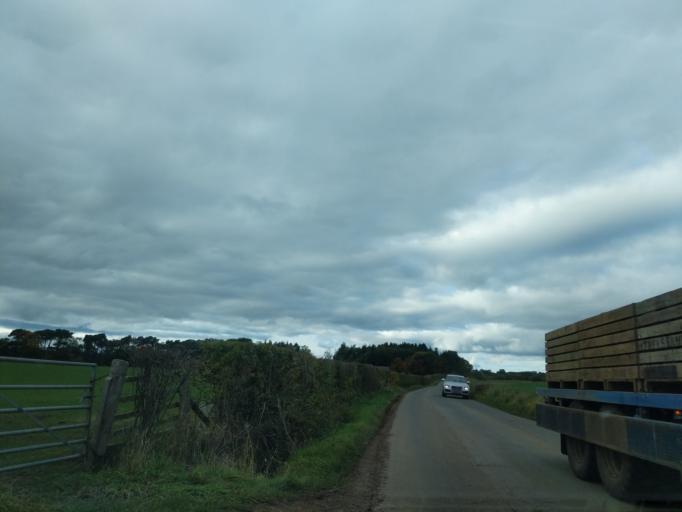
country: GB
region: Scotland
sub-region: East Lothian
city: Haddington
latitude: 55.9374
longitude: -2.8387
